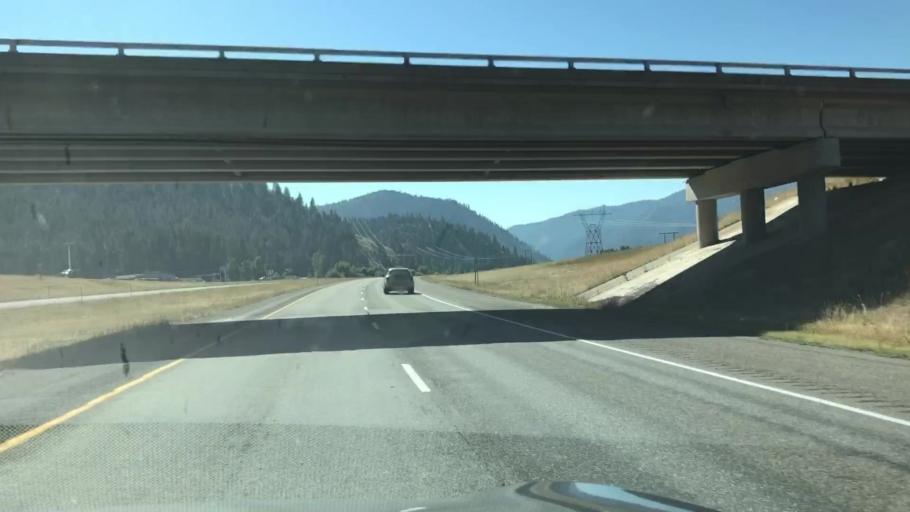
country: US
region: Montana
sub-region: Missoula County
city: Clinton
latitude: 46.7791
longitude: -113.7145
